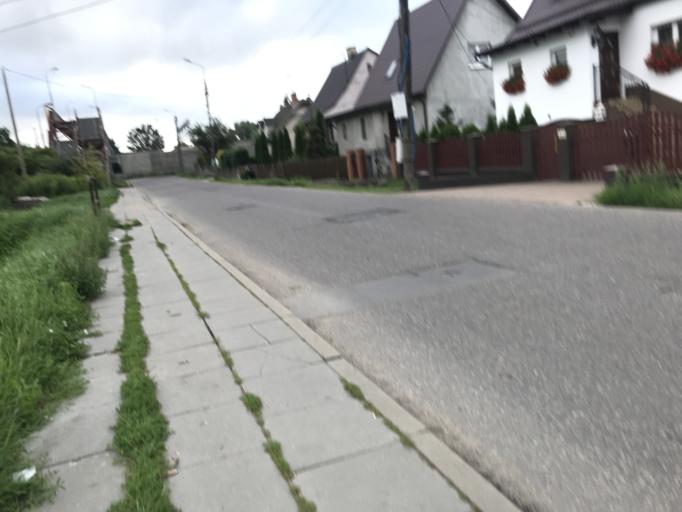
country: PL
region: Pomeranian Voivodeship
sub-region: Gdansk
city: Gdansk
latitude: 54.3371
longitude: 18.6751
